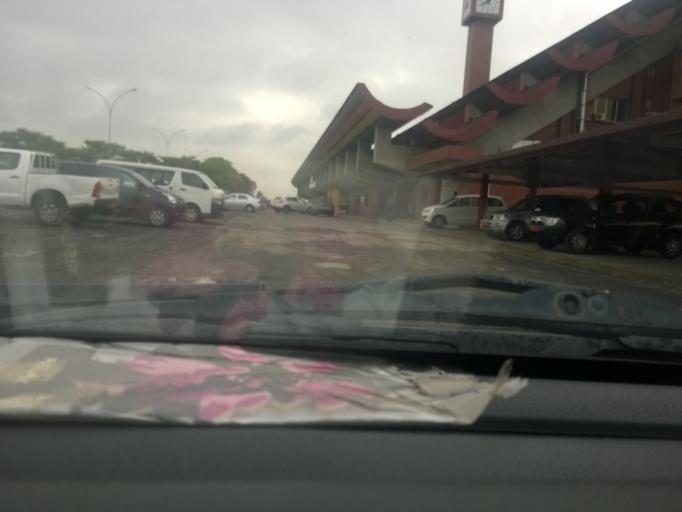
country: CM
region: Littoral
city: Douala
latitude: 4.0545
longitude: 9.7108
